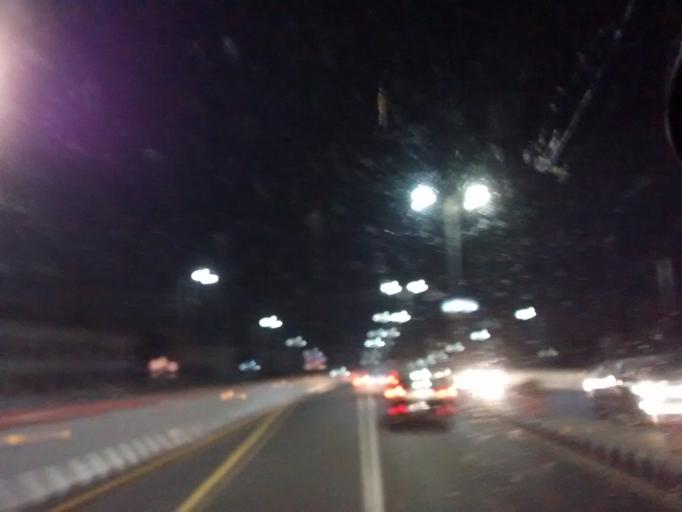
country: IN
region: Telangana
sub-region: Hyderabad
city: Hyderabad
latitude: 17.3479
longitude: 78.4164
